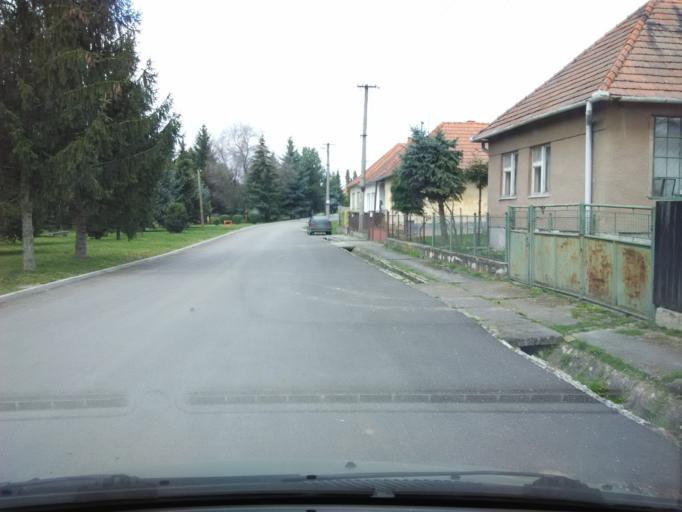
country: SK
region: Nitriansky
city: Zlate Moravce
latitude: 48.4180
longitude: 18.3572
